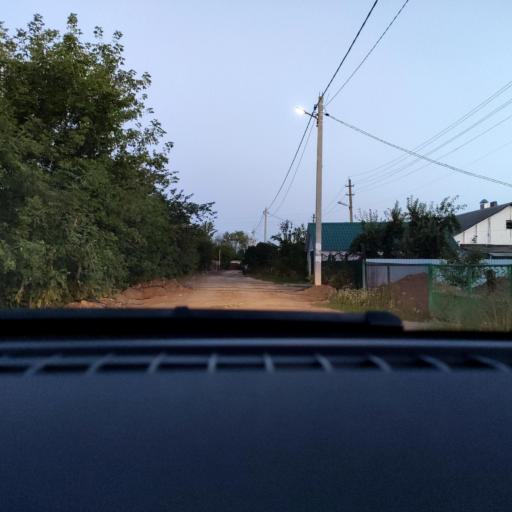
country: RU
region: Voronezj
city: Ramon'
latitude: 51.9295
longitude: 39.2512
